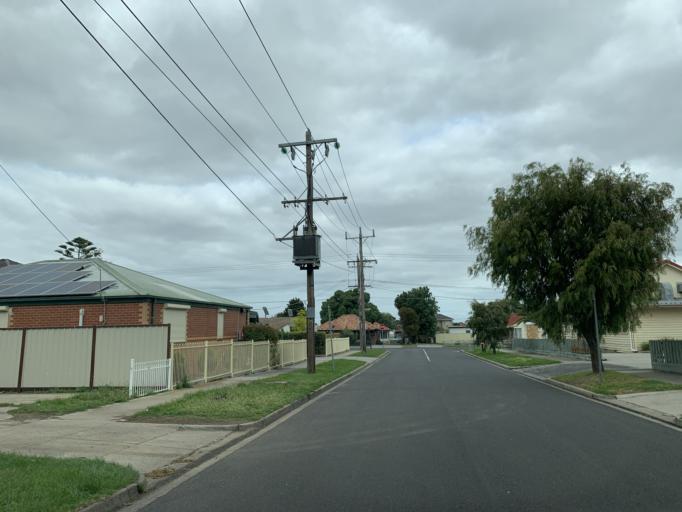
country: AU
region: Victoria
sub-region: Brimbank
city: St Albans
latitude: -37.7443
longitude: 144.8051
